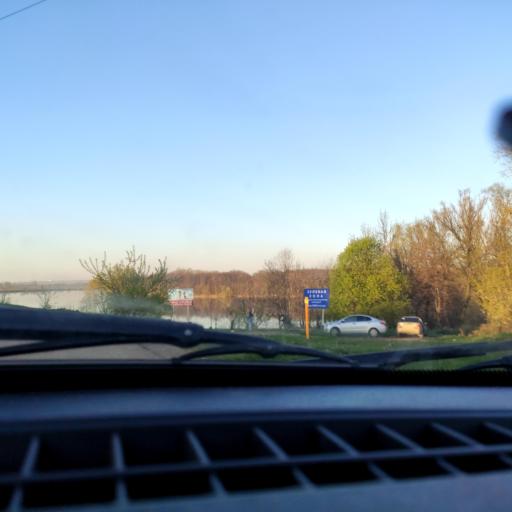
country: RU
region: Bashkortostan
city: Mikhaylovka
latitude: 54.8087
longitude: 55.8974
